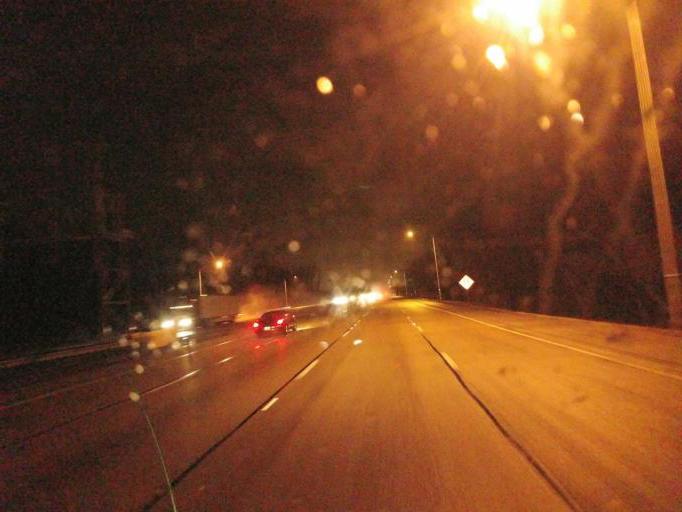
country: US
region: Illinois
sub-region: Saint Clair County
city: Caseyville
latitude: 38.6695
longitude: -90.0422
